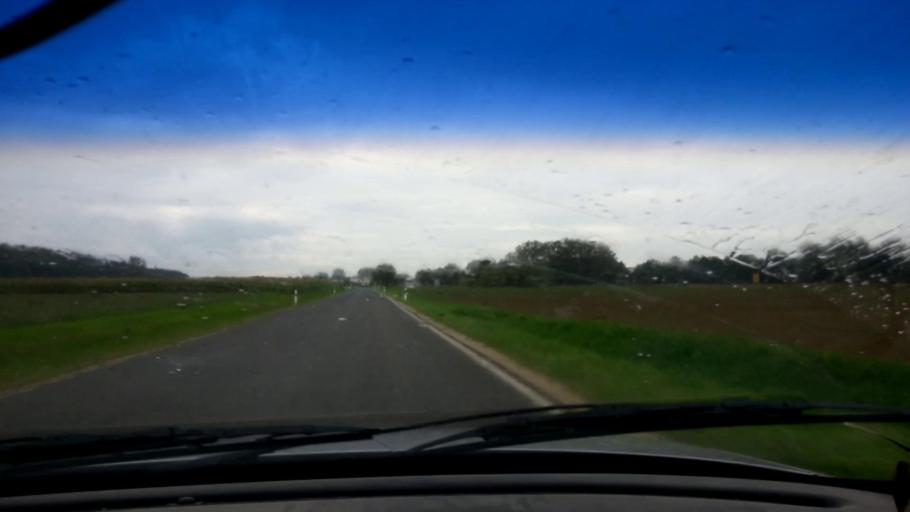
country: DE
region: Bavaria
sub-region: Upper Franconia
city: Memmelsdorf
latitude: 49.9423
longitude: 10.9826
